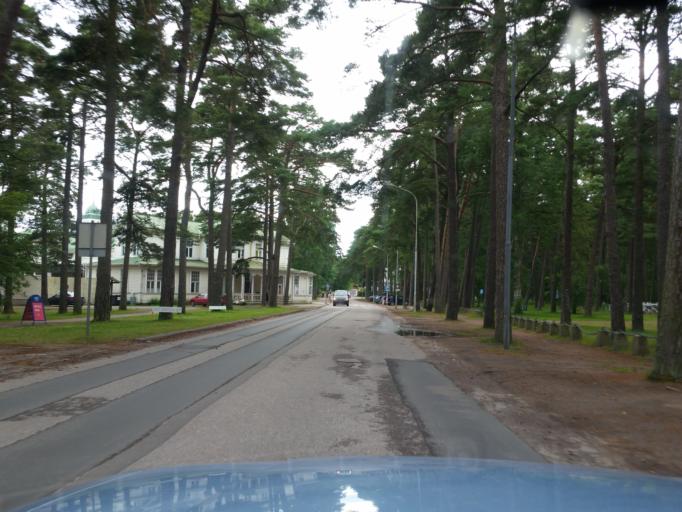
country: FI
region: Uusimaa
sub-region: Raaseporin
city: Hanko
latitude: 59.8249
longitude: 22.9790
